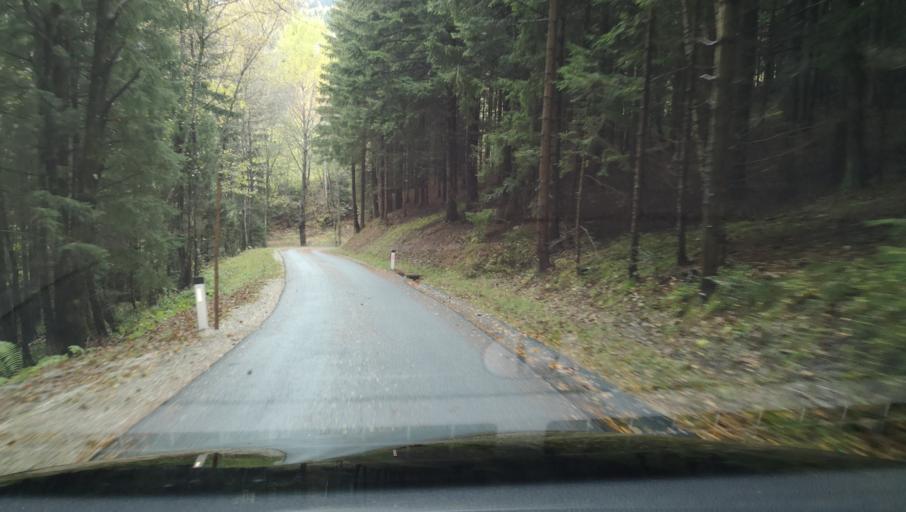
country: AT
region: Styria
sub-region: Politischer Bezirk Weiz
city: Gasen
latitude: 47.3579
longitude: 15.6079
